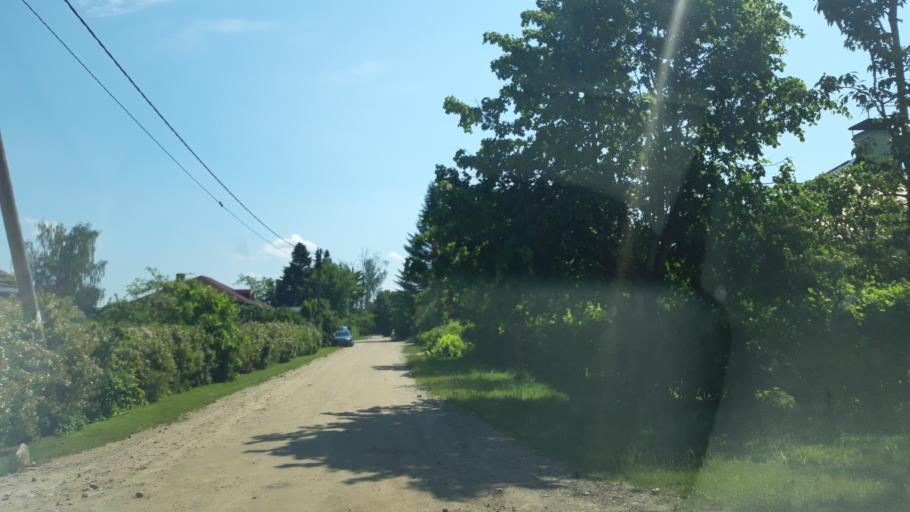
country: LV
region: Saulkrastu
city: Saulkrasti
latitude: 57.2569
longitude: 24.4117
